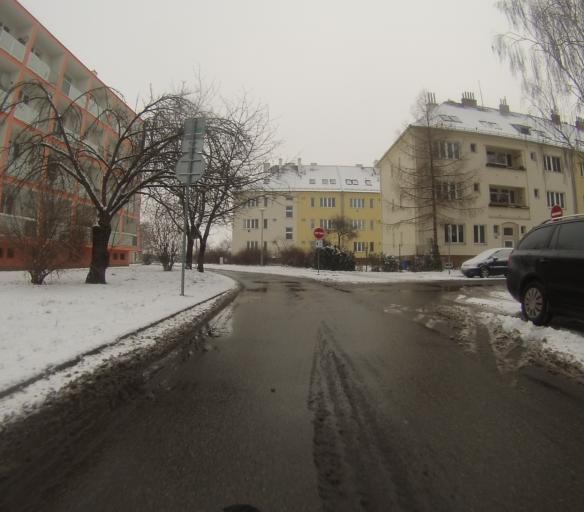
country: CZ
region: South Moravian
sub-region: Mesto Brno
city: Brno
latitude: 49.1752
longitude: 16.6279
